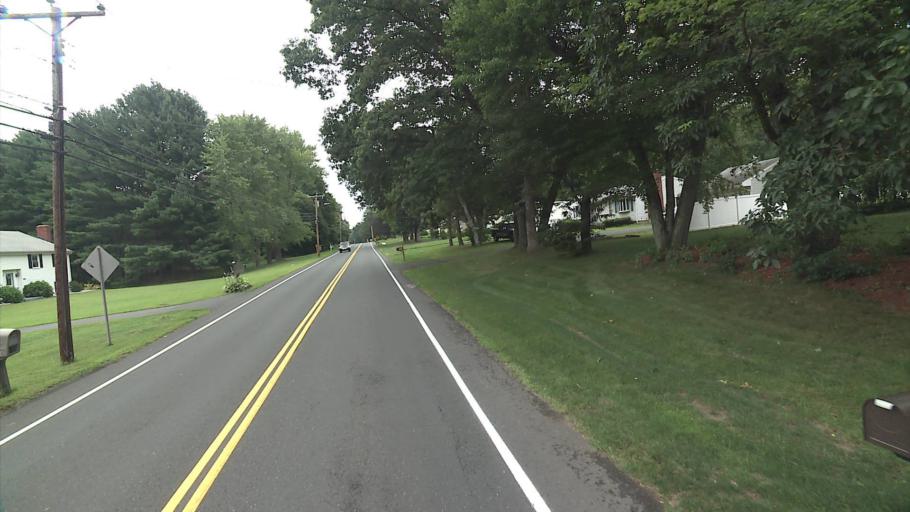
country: US
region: Connecticut
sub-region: Hartford County
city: Manchester
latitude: 41.8374
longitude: -72.5398
